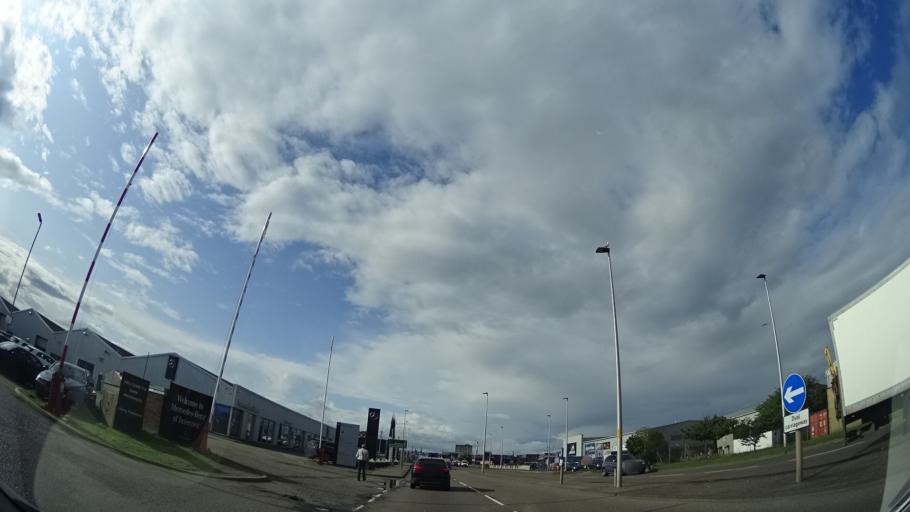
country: GB
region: Scotland
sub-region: Highland
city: Inverness
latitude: 57.4894
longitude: -4.2186
